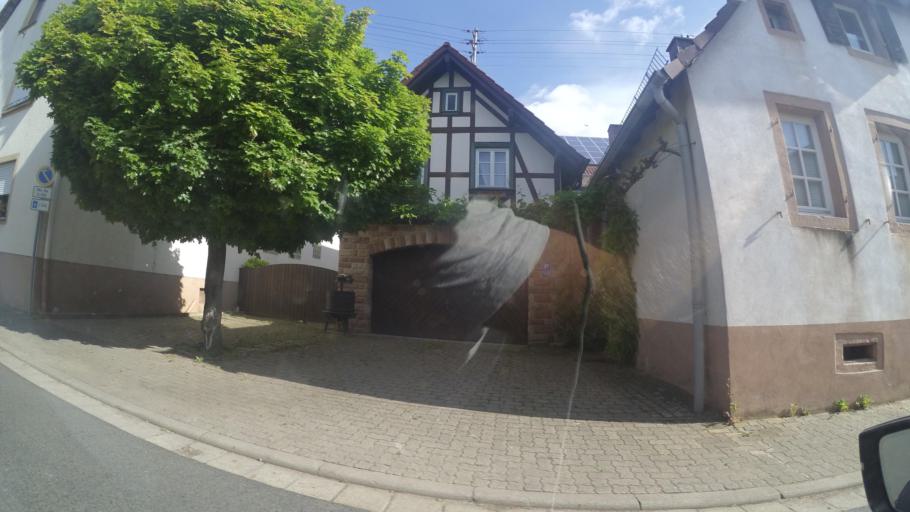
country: DE
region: Rheinland-Pfalz
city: Gocklingen
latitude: 49.1621
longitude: 8.0380
